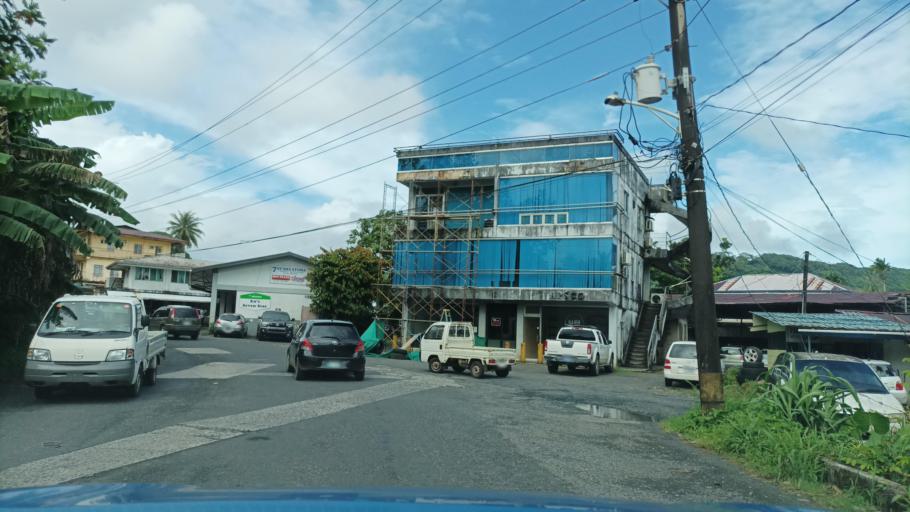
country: FM
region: Pohnpei
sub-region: Kolonia Municipality
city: Kolonia
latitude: 6.9584
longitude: 158.2072
